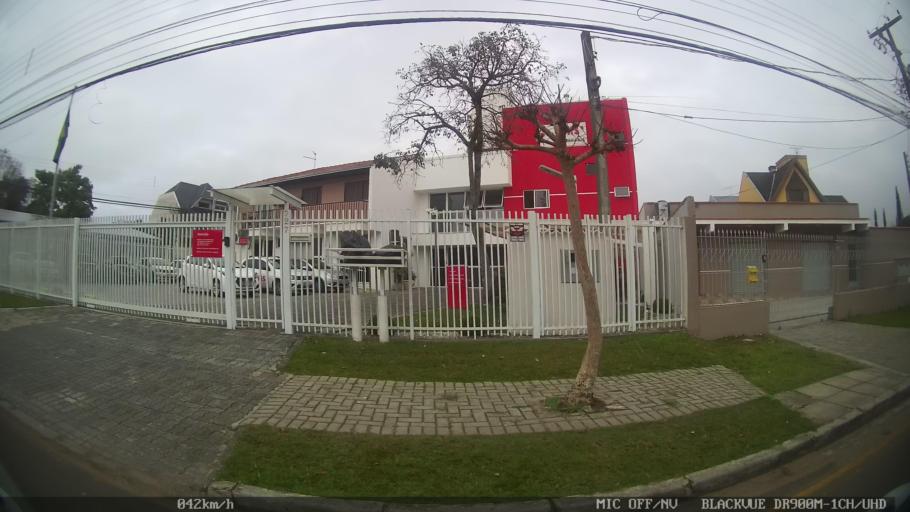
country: BR
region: Parana
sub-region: Almirante Tamandare
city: Almirante Tamandare
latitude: -25.3791
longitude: -49.3278
